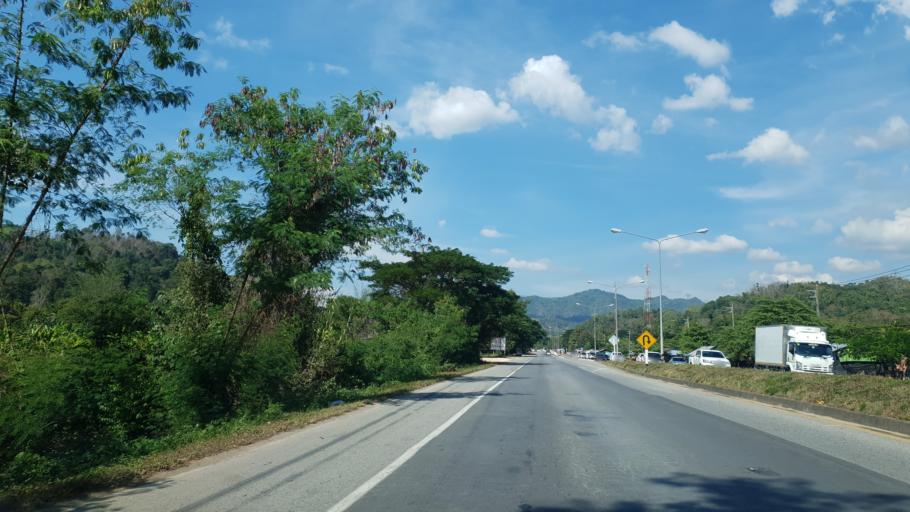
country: TH
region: Uttaradit
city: Lap Lae
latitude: 17.7947
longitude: 100.1162
